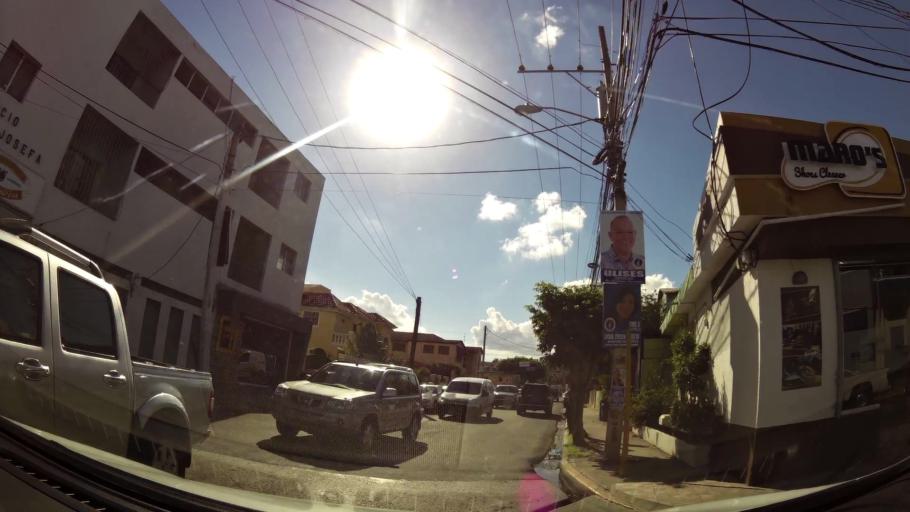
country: DO
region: Santiago
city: Santiago de los Caballeros
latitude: 19.4511
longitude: -70.6780
